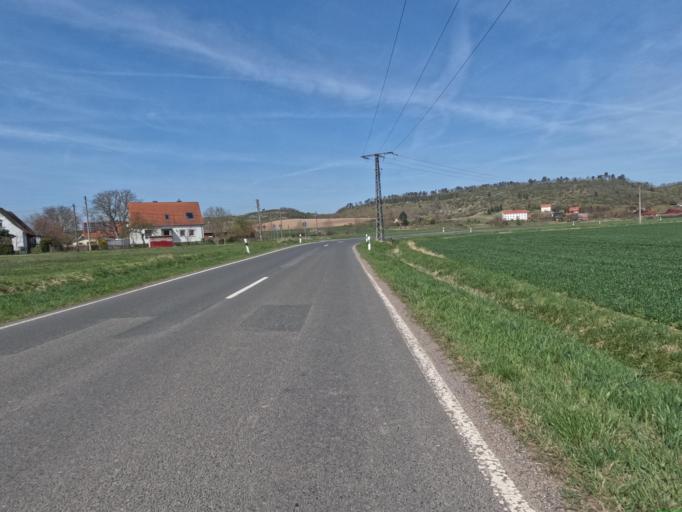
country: DE
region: Saxony-Anhalt
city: Beesenstedt
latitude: 51.6126
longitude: 11.7390
